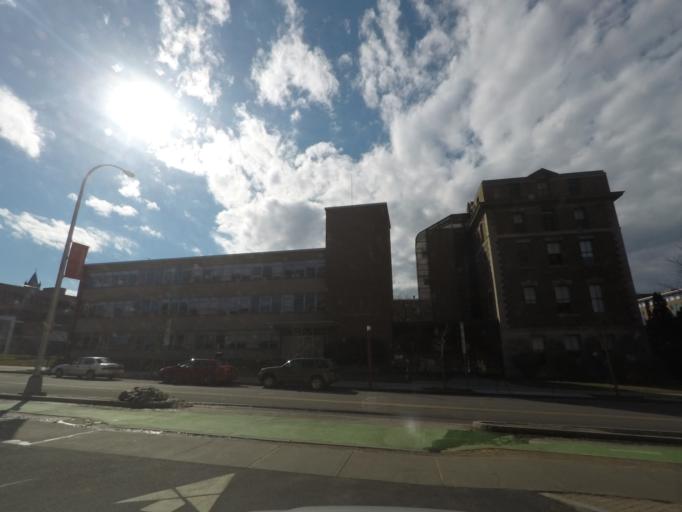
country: US
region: New York
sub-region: Onondaga County
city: Syracuse
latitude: 43.0412
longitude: -76.1343
